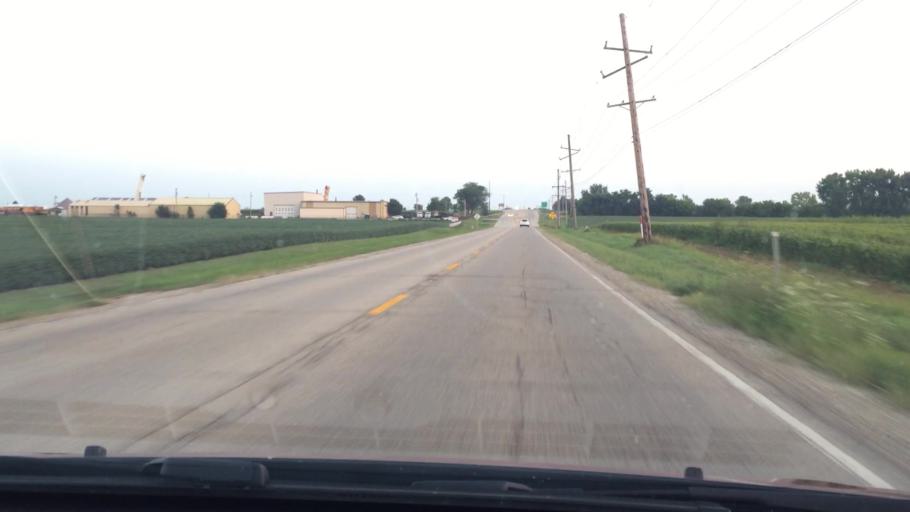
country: US
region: Illinois
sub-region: Bureau County
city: Ladd
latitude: 41.3755
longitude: -89.2190
